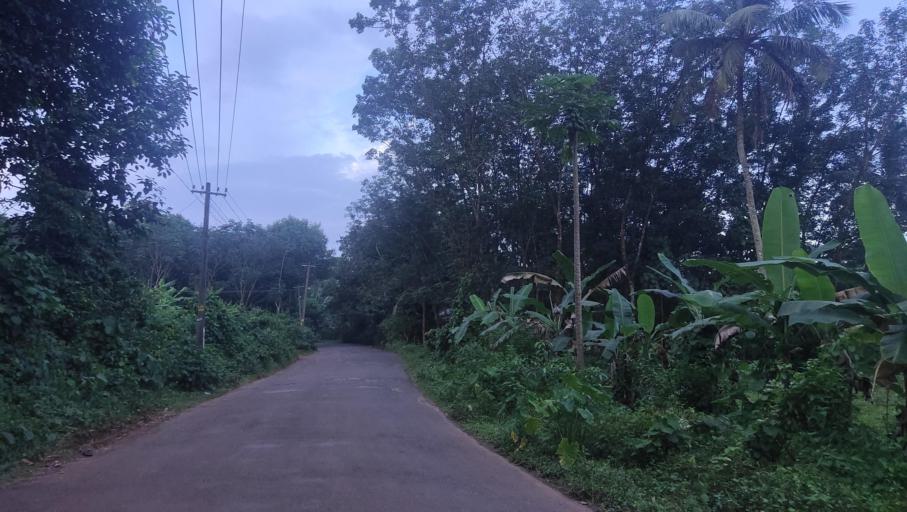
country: IN
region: Kerala
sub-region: Alappuzha
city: Kattanam
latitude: 9.1338
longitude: 76.6356
